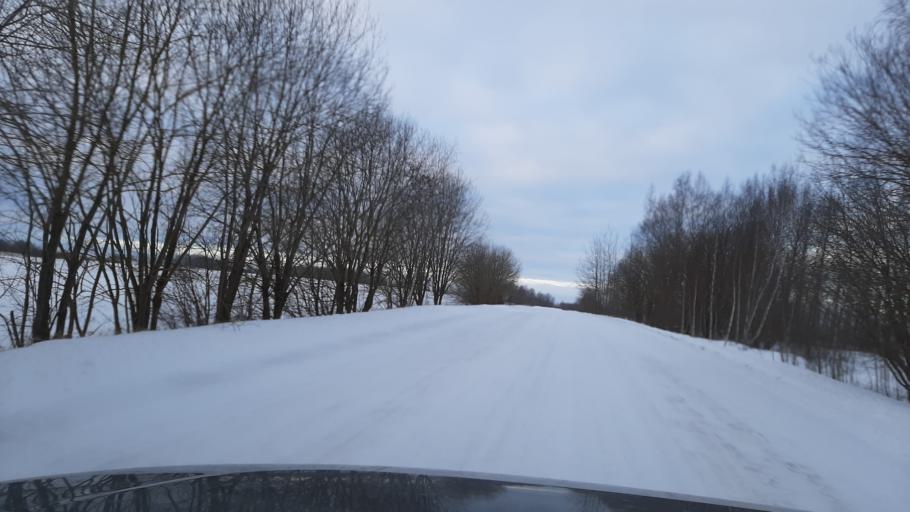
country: RU
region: Kostroma
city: Kosmynino
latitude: 57.4783
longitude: 40.8638
